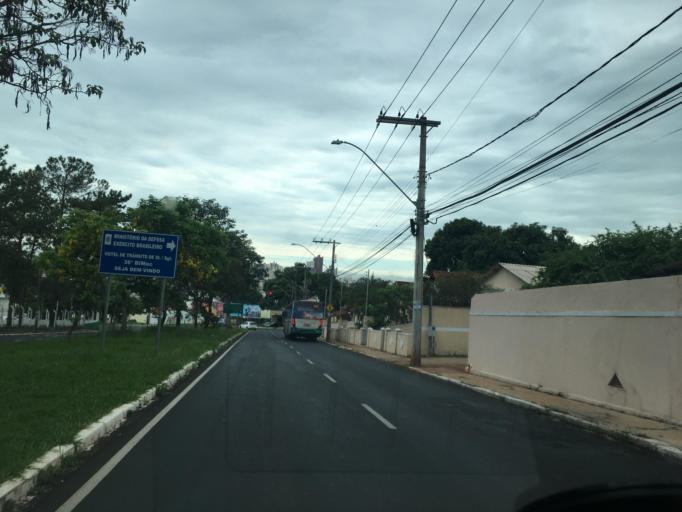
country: BR
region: Minas Gerais
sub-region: Uberlandia
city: Uberlandia
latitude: -18.9266
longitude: -48.3047
